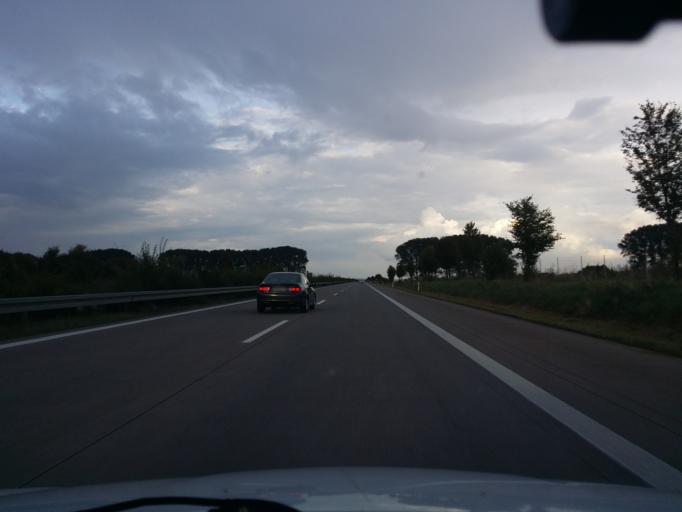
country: DE
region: Saxony-Anhalt
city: Bornstedt
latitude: 51.4374
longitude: 11.4437
